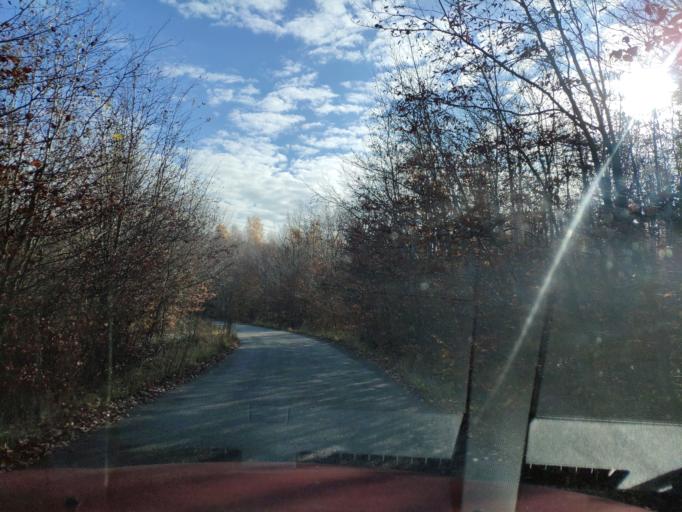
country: SK
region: Kosicky
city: Secovce
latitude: 48.6264
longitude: 21.4583
